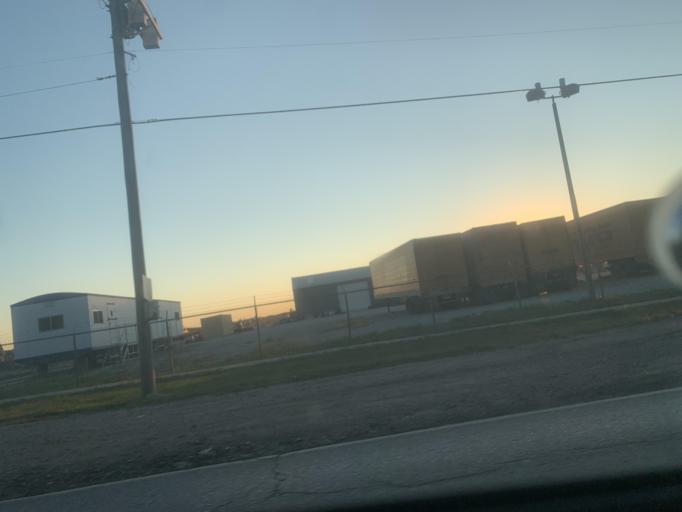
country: US
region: Nebraska
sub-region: Sarpy County
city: La Vista
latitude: 41.2017
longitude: -96.0047
